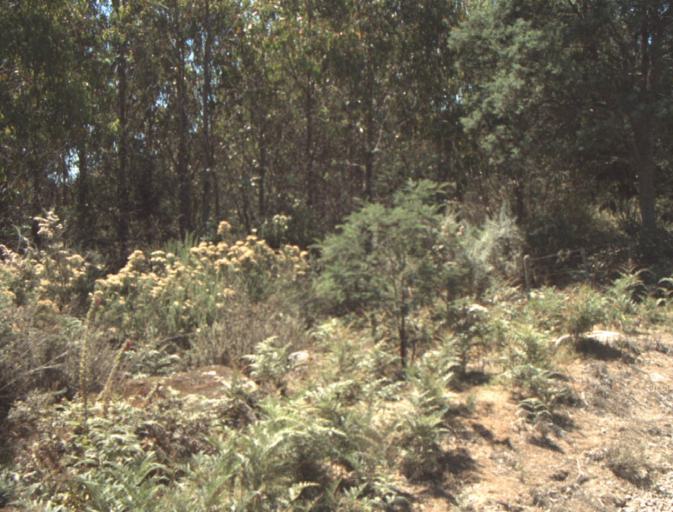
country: AU
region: Tasmania
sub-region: Dorset
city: Scottsdale
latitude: -41.3199
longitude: 147.4592
